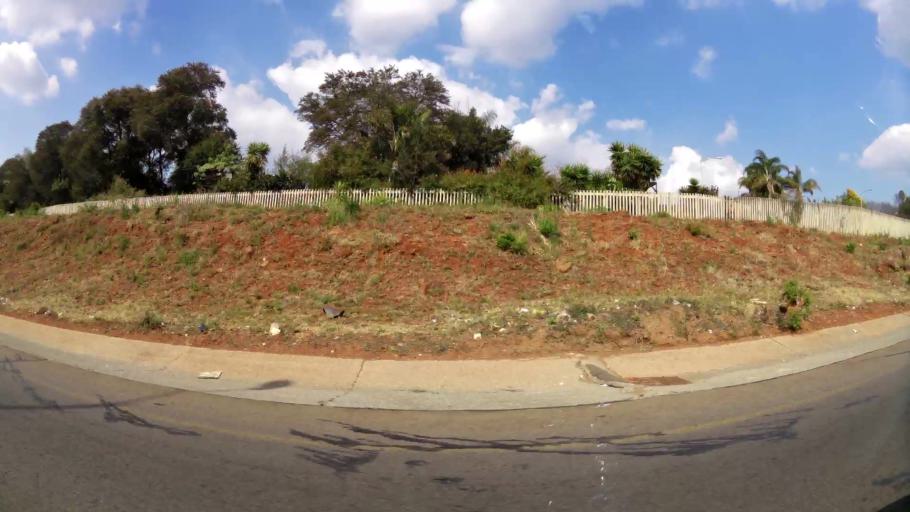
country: ZA
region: Gauteng
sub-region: City of Tshwane Metropolitan Municipality
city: Centurion
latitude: -25.8056
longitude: 28.2932
